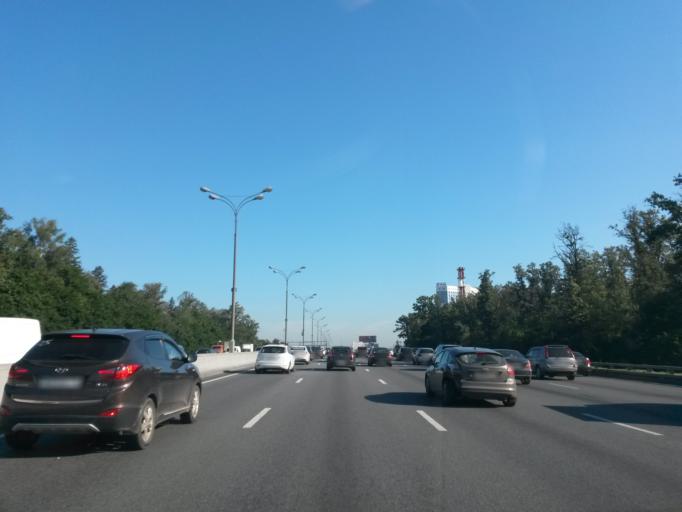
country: RU
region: Moscow
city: Vostochnyy
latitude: 55.7996
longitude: 37.8404
